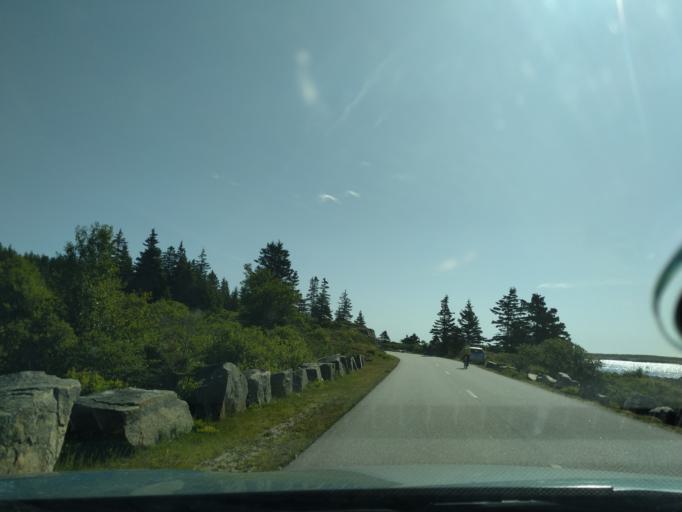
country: US
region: Maine
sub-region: Hancock County
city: Gouldsboro
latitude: 44.3384
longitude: -68.0493
